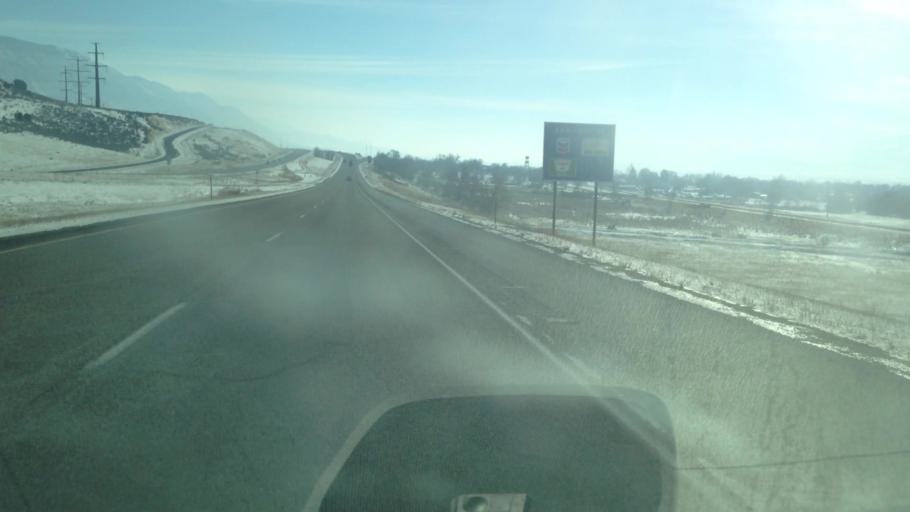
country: US
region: Idaho
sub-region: Oneida County
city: Malad City
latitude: 42.1967
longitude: -112.2378
